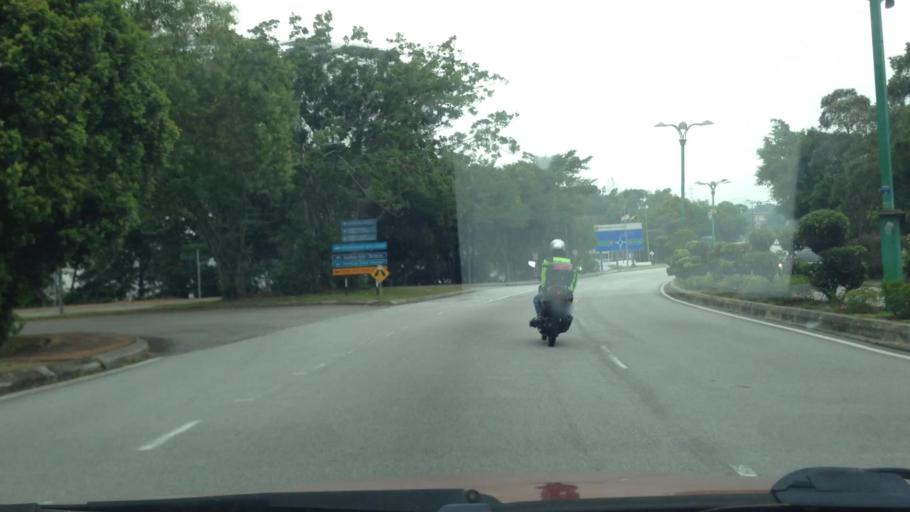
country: MY
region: Selangor
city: Shah Alam
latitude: 3.0727
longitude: 101.5371
